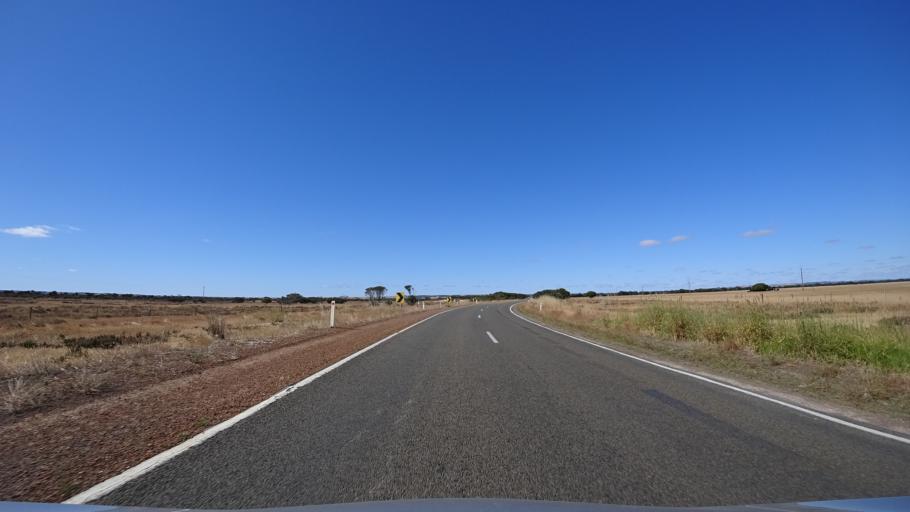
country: AU
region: South Australia
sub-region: Kangaroo Island
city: Kingscote
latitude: -35.6993
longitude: 137.5705
